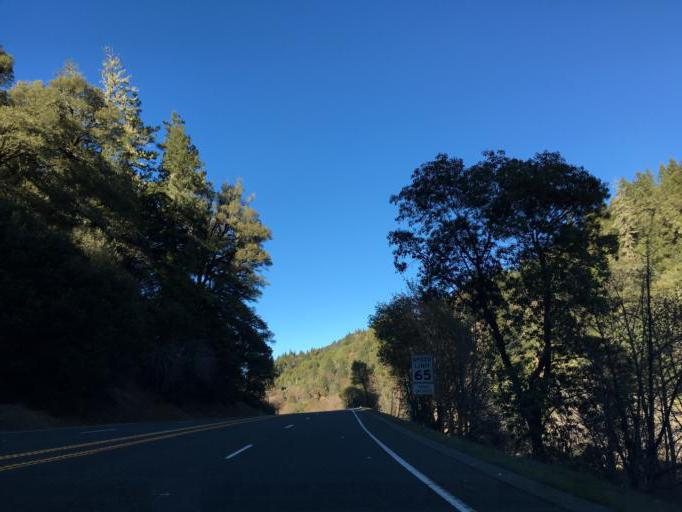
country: US
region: California
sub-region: Mendocino County
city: Brooktrails
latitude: 39.5584
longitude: -123.4328
